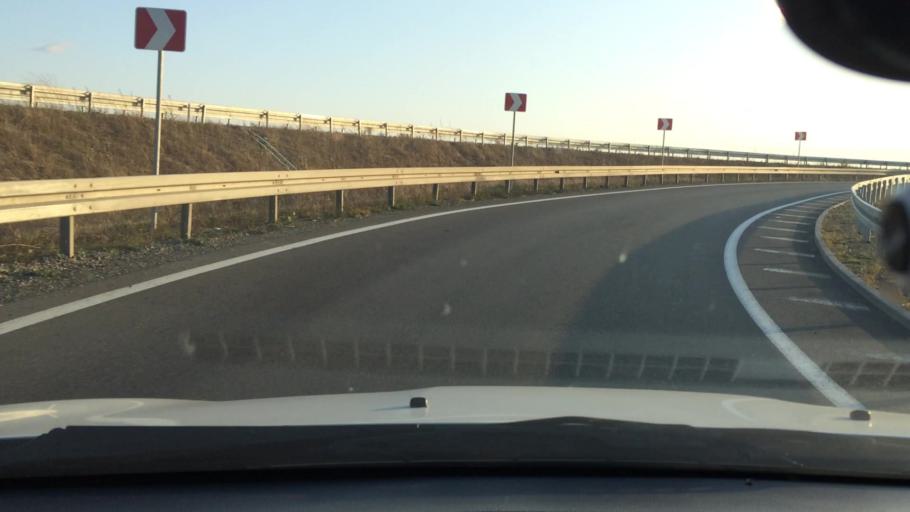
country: GE
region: Shida Kartli
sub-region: Khashuris Raioni
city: Khashuri
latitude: 42.0122
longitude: 43.6991
